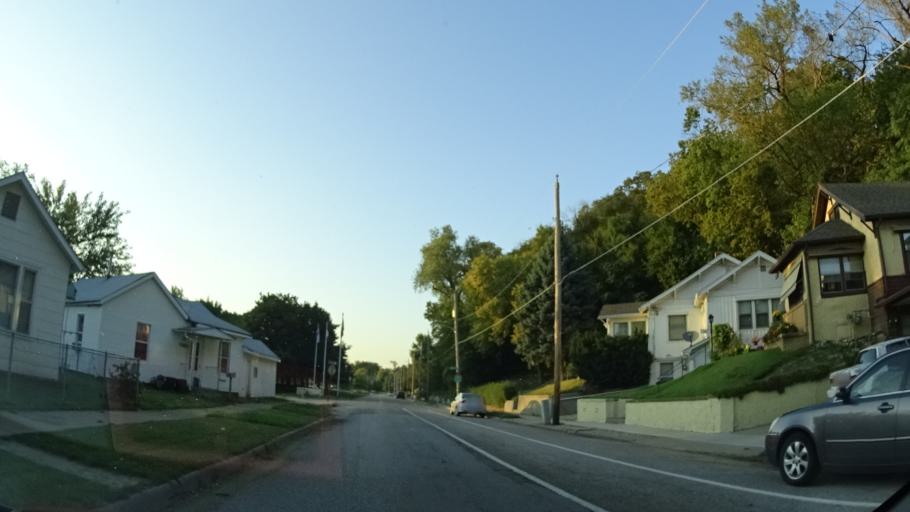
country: US
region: Iowa
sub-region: Pottawattamie County
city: Council Bluffs
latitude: 41.2657
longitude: -95.8519
